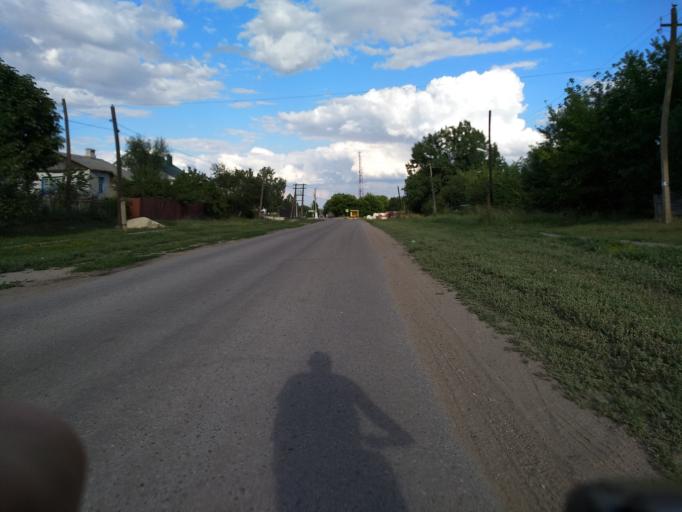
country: RU
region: Lipetsk
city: Dobrinka
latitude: 52.0376
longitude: 40.5483
